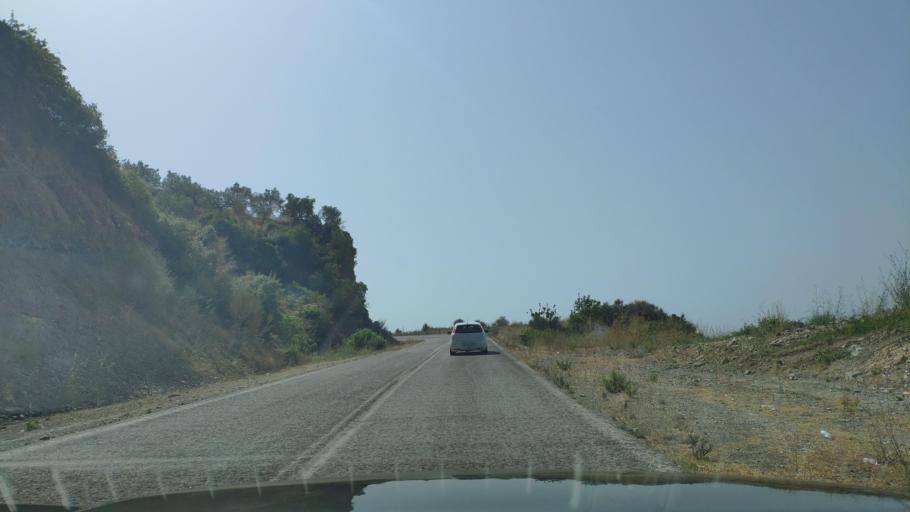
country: GR
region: Epirus
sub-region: Nomos Artas
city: Peta
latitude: 39.1691
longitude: 21.0458
